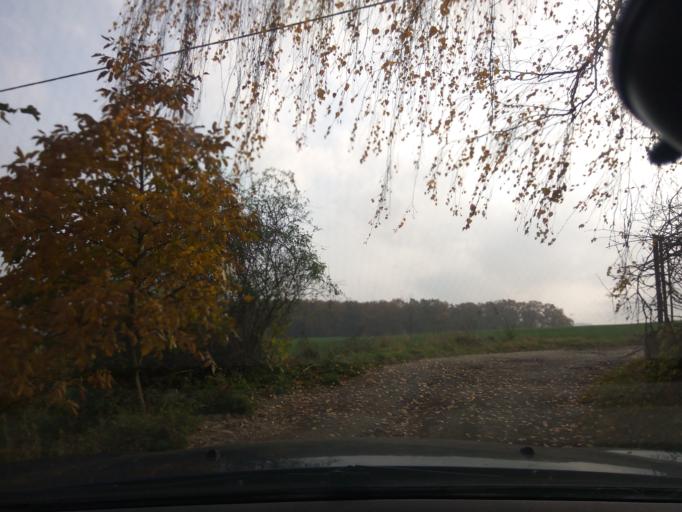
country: SK
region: Trnavsky
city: Vrbove
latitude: 48.6679
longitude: 17.6607
